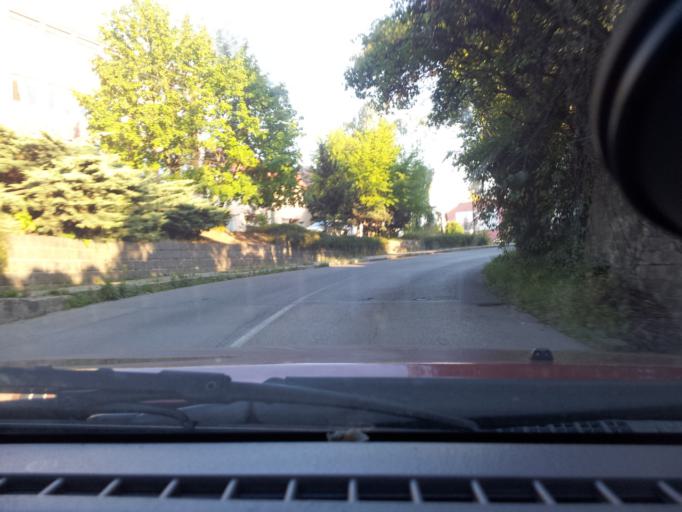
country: CZ
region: South Moravian
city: Hodonin
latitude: 48.8575
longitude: 17.1247
